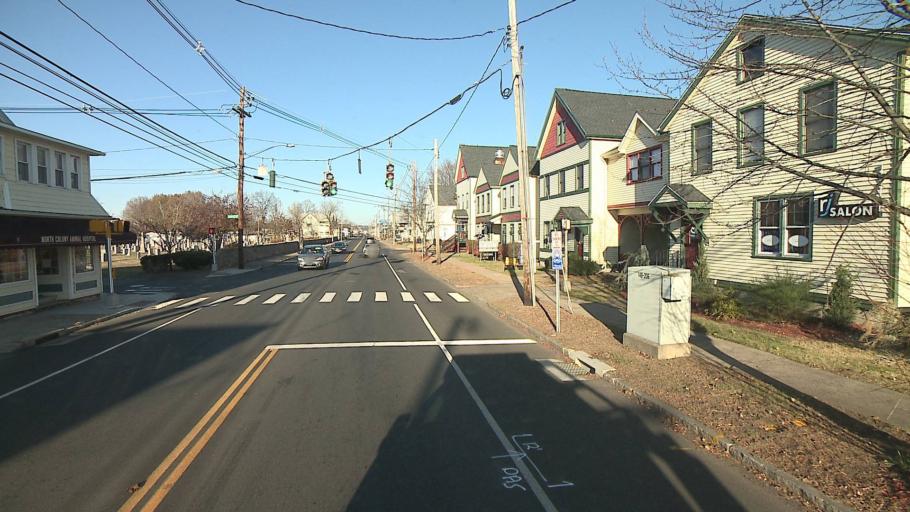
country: US
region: Connecticut
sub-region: New Haven County
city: Wallingford
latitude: 41.4622
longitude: -72.8209
